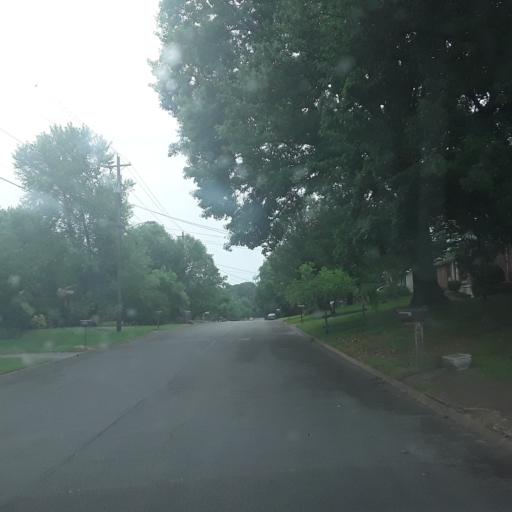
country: US
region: Tennessee
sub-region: Williamson County
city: Brentwood
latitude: 36.0598
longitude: -86.7341
